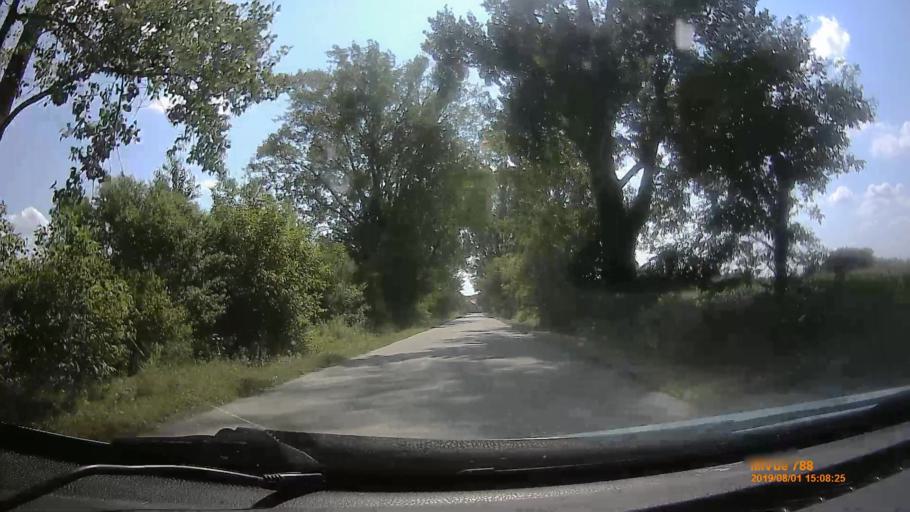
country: HU
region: Baranya
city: Sellye
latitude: 45.8514
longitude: 17.8188
